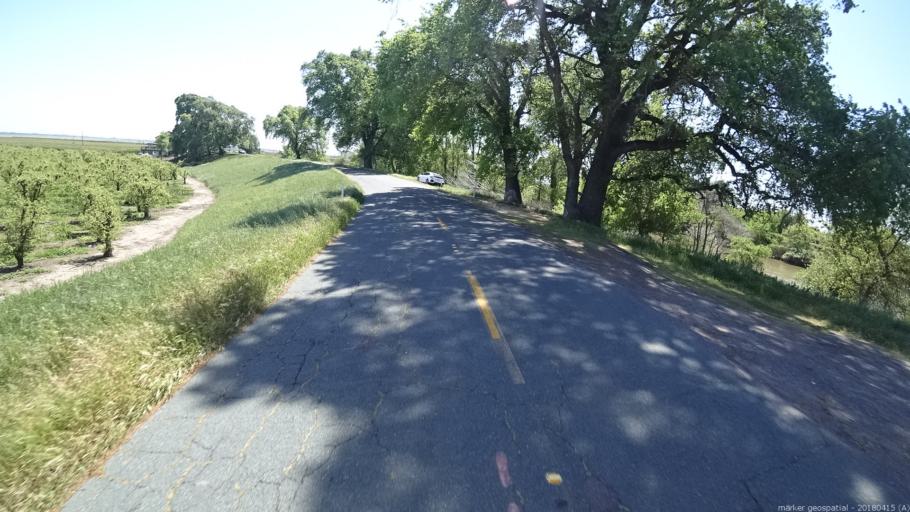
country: US
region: California
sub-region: Sacramento County
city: Walnut Grove
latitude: 38.2761
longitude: -121.5901
